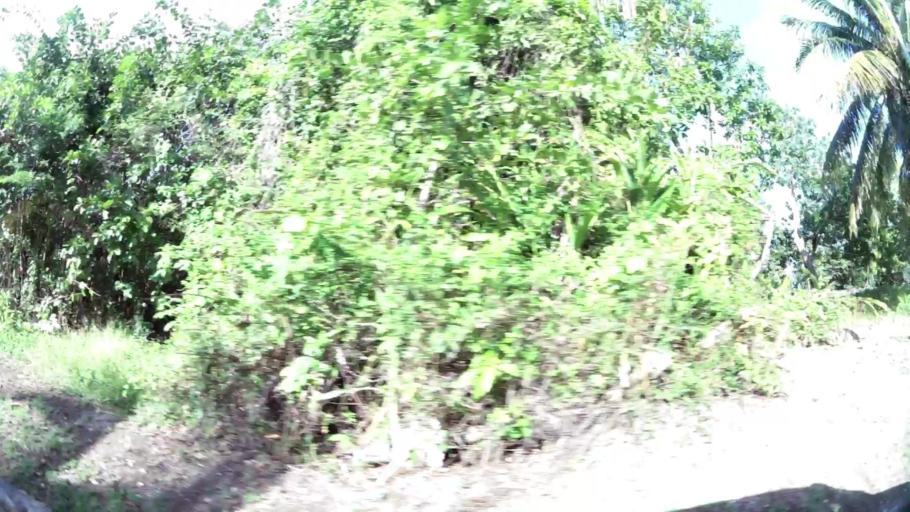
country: AG
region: Saint Peter
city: All Saints
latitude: 17.0510
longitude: -61.8071
